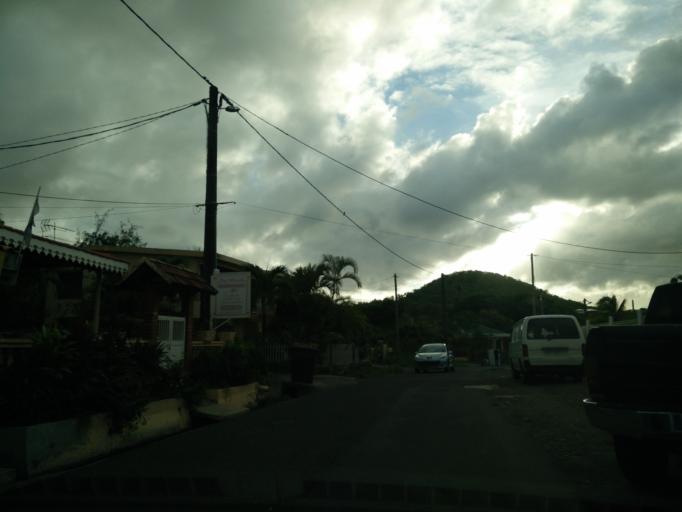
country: MQ
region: Martinique
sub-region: Martinique
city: Le Marin
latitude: 14.4599
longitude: -60.8459
